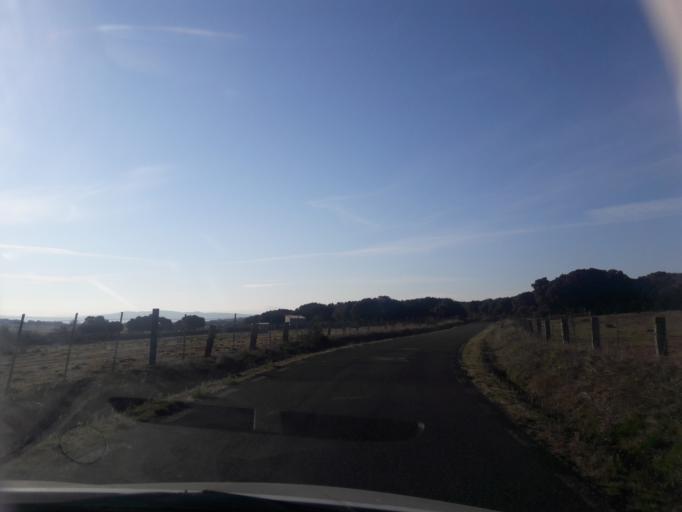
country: ES
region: Castille and Leon
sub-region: Provincia de Salamanca
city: Montejo
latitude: 40.6232
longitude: -5.6103
